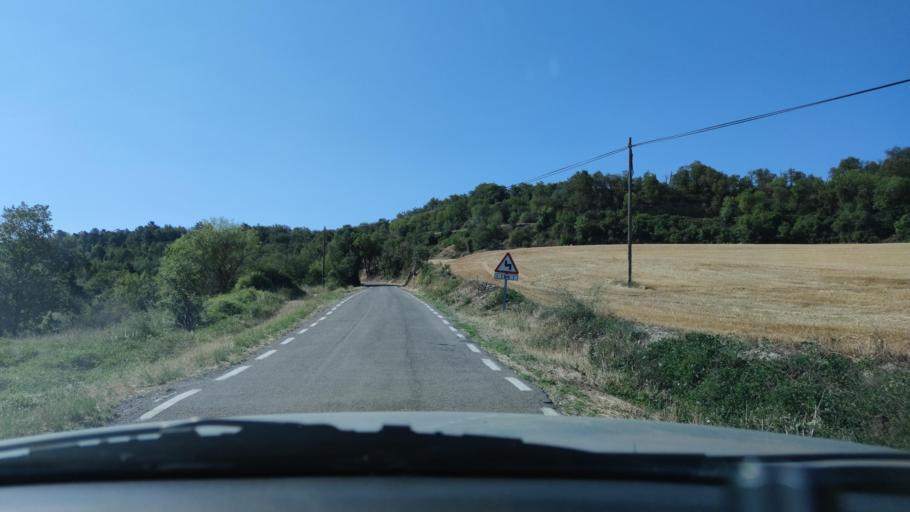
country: ES
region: Catalonia
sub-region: Provincia de Lleida
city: Ivorra
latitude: 41.7356
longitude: 1.3553
